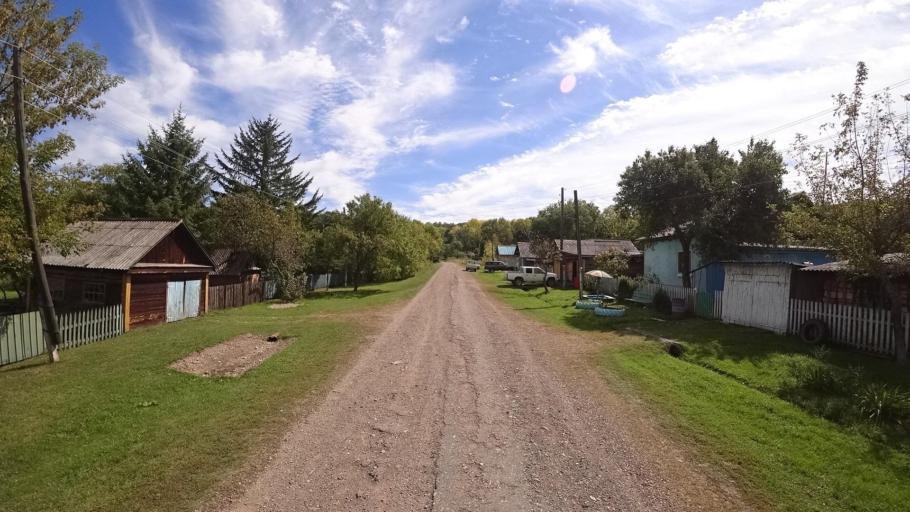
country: RU
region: Primorskiy
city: Yakovlevka
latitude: 44.6535
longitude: 133.7472
